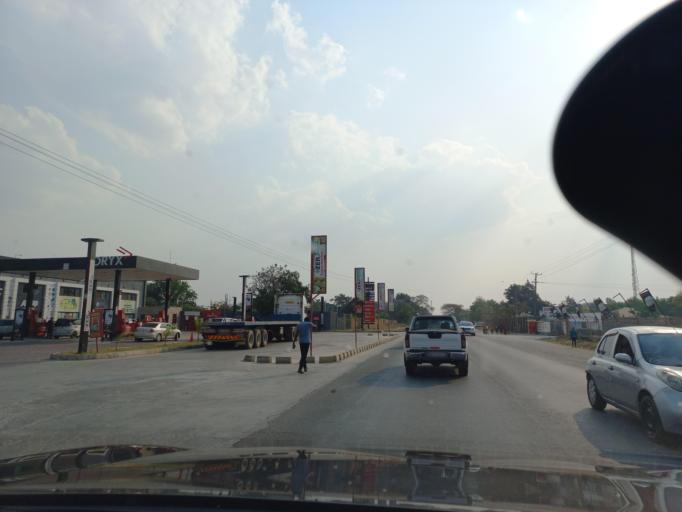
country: ZM
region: Lusaka
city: Lusaka
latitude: -15.4578
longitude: 28.2591
